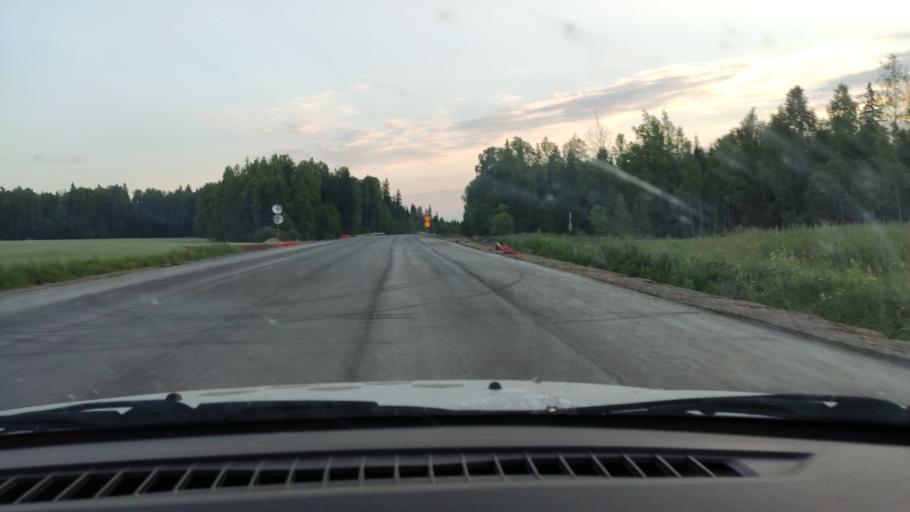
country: RU
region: Perm
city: Siva
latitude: 58.4653
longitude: 54.4067
